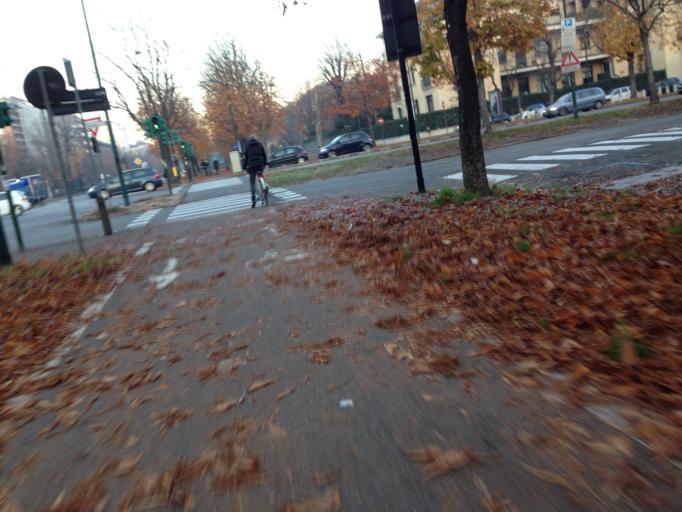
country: IT
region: Piedmont
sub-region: Provincia di Torino
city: Turin
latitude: 45.0633
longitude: 7.6699
